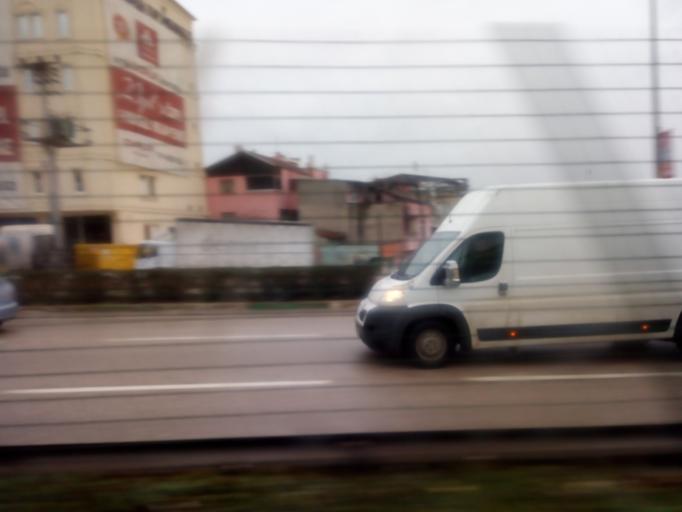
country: TR
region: Bursa
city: Yildirim
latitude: 40.2275
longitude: 28.9888
